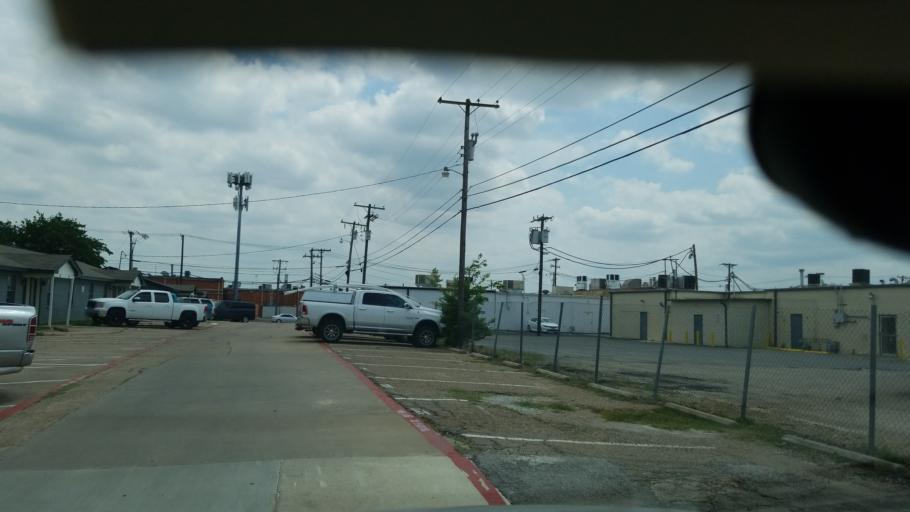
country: US
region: Texas
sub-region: Dallas County
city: Irving
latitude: 32.8465
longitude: -96.9582
